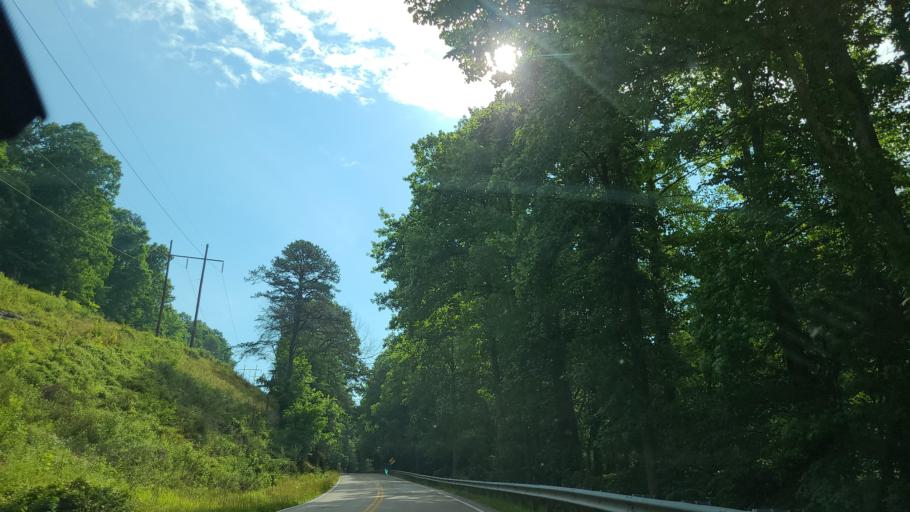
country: US
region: Kentucky
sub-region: Knox County
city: Barbourville
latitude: 36.6857
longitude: -83.8849
